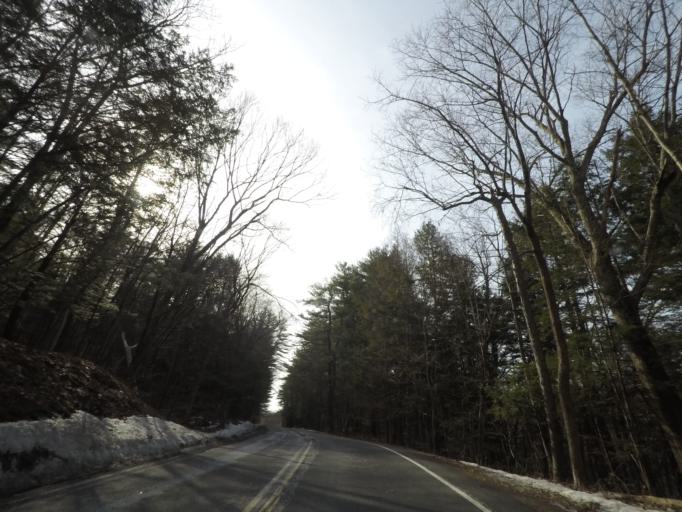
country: US
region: New York
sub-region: Rensselaer County
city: Nassau
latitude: 42.4857
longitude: -73.5602
